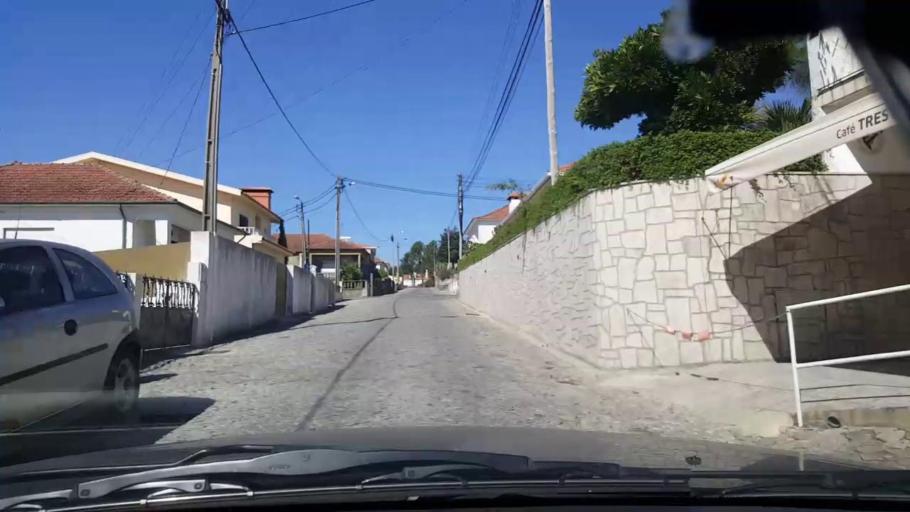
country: PT
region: Porto
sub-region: Vila do Conde
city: Arvore
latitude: 41.3174
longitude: -8.6739
